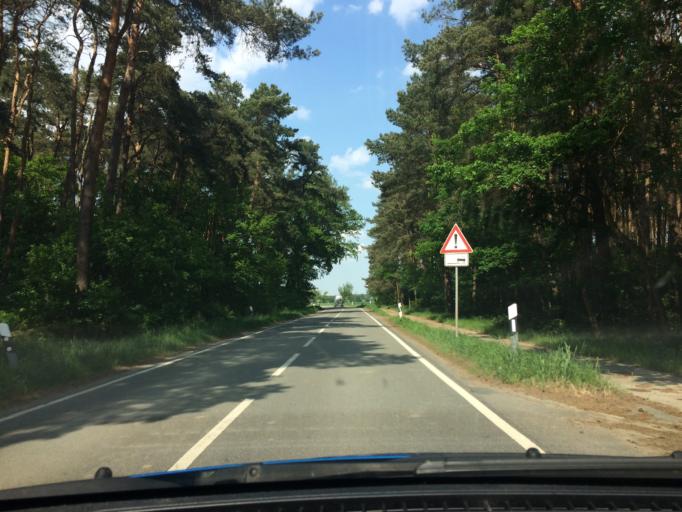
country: DE
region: Lower Saxony
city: Neu Darchau
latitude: 53.2648
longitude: 10.9205
